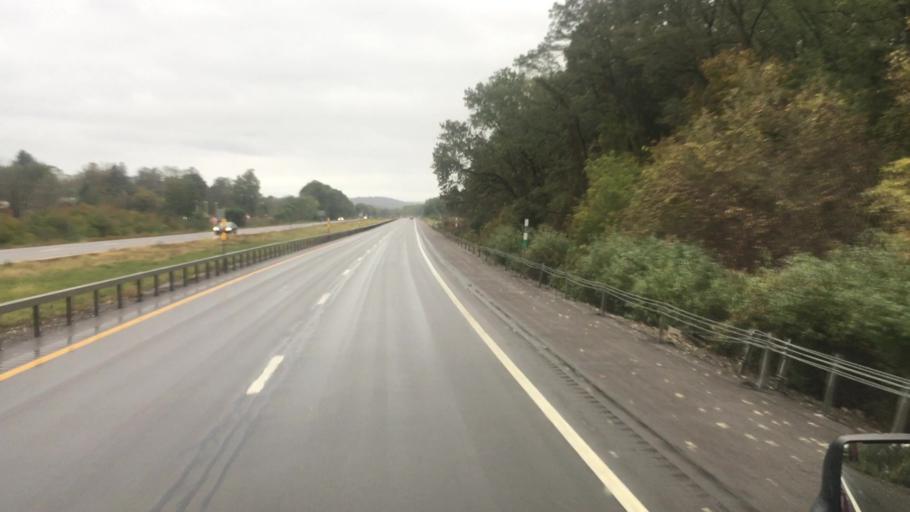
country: US
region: New York
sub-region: Broome County
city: Endicott
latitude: 42.0704
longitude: -76.0971
